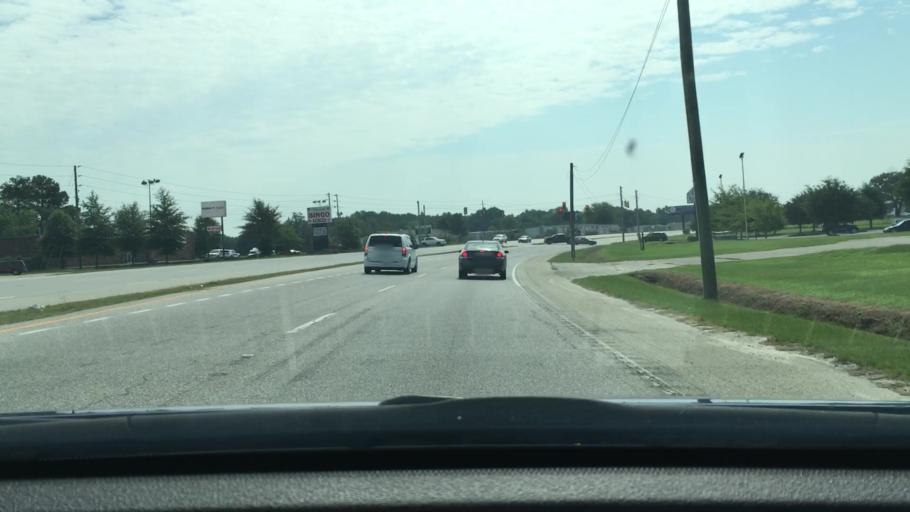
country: US
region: South Carolina
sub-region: Sumter County
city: Cherryvale
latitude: 33.9653
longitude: -80.4082
